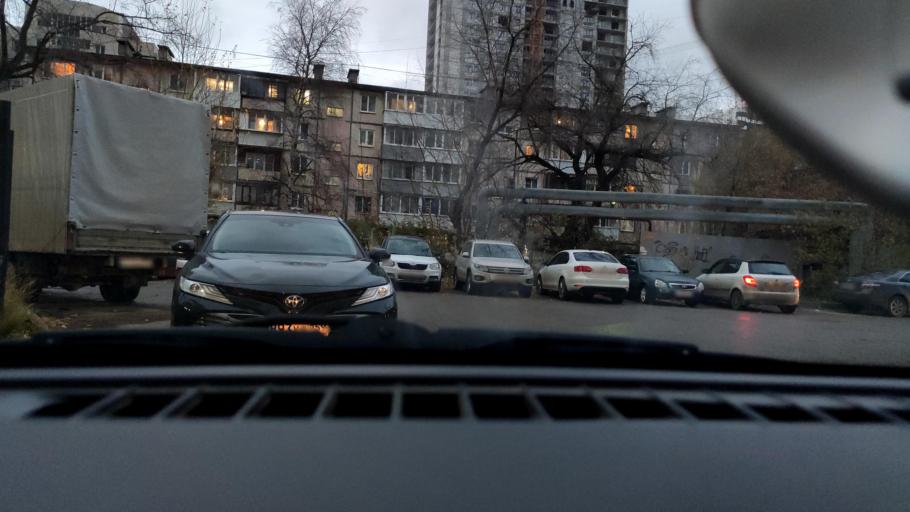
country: RU
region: Perm
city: Perm
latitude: 57.9971
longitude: 56.2680
